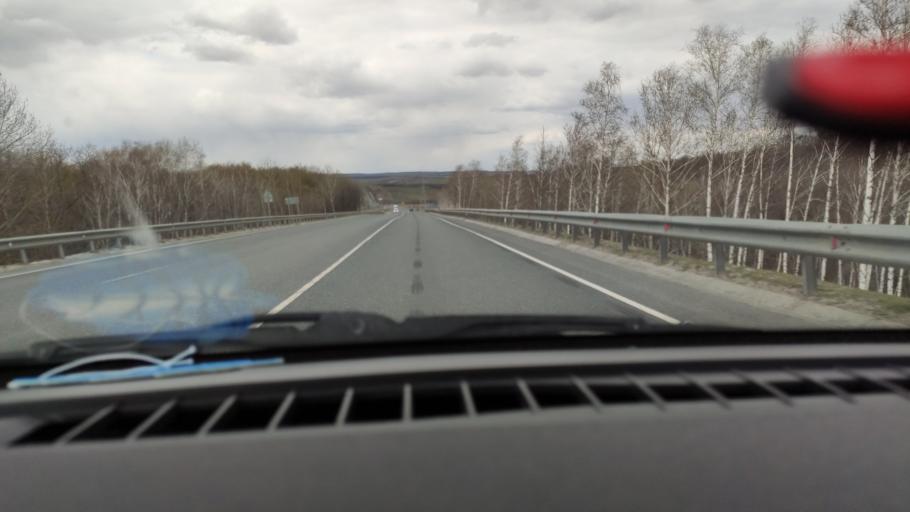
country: RU
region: Saratov
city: Vol'sk
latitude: 52.1144
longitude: 47.3063
